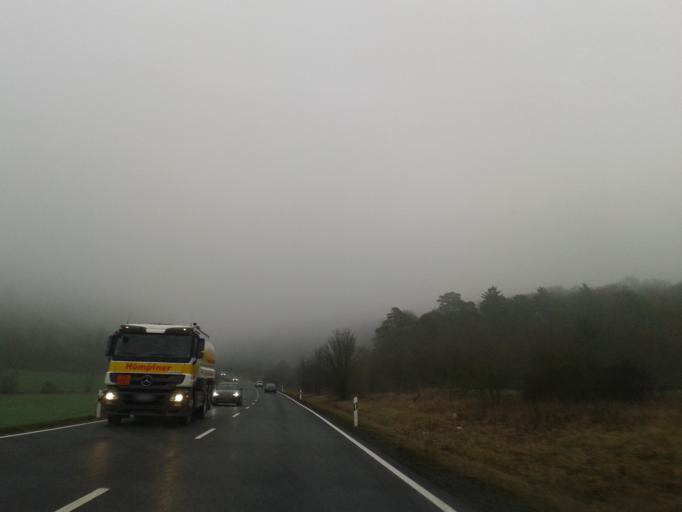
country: DE
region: Bavaria
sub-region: Regierungsbezirk Unterfranken
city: Hofheim in Unterfranken
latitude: 50.1264
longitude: 10.5728
